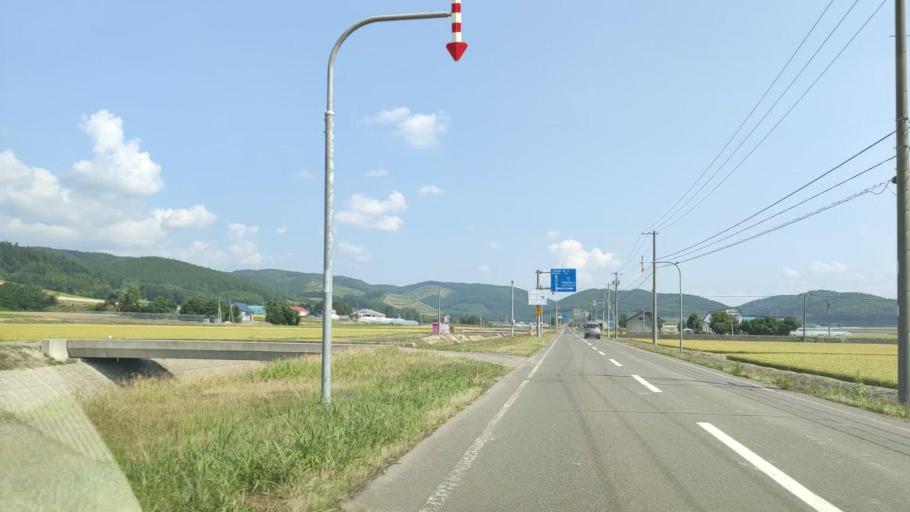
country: JP
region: Hokkaido
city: Shimo-furano
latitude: 43.4020
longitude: 142.3941
